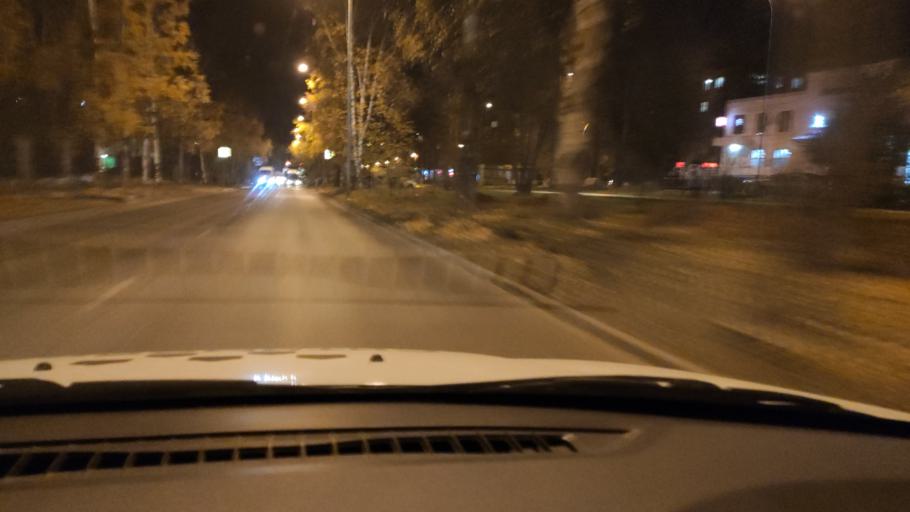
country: RU
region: Perm
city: Perm
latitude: 57.9798
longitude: 56.1827
